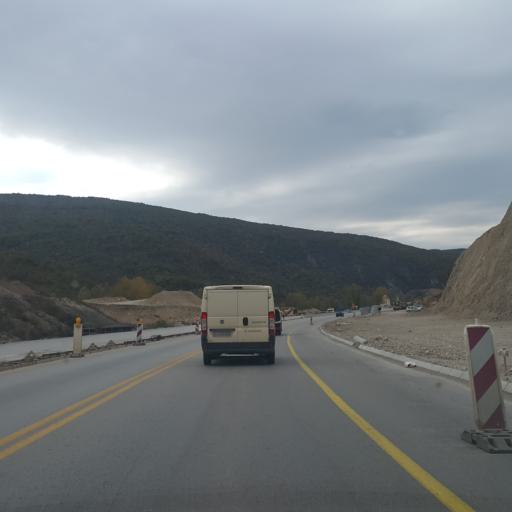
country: RS
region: Central Serbia
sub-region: Pirotski Okrug
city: Bela Palanka
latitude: 43.2243
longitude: 22.4286
